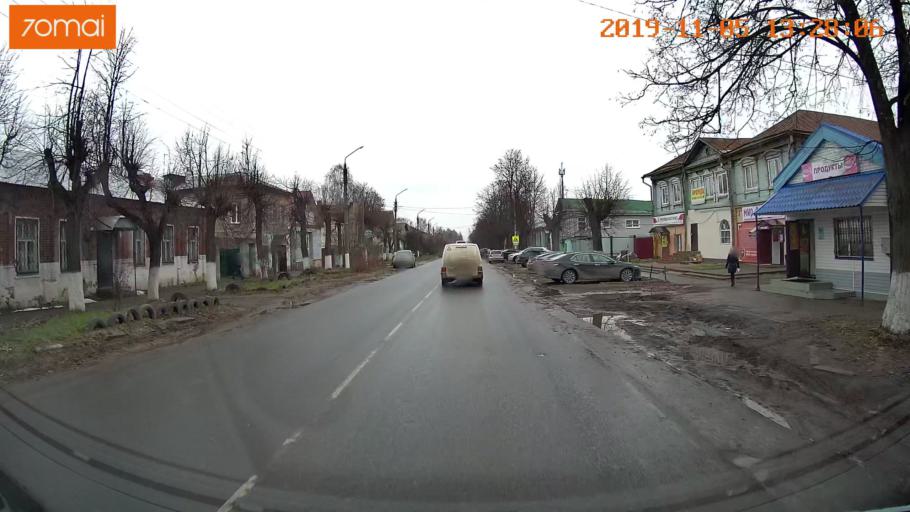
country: RU
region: Ivanovo
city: Shuya
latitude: 56.8558
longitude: 41.3849
